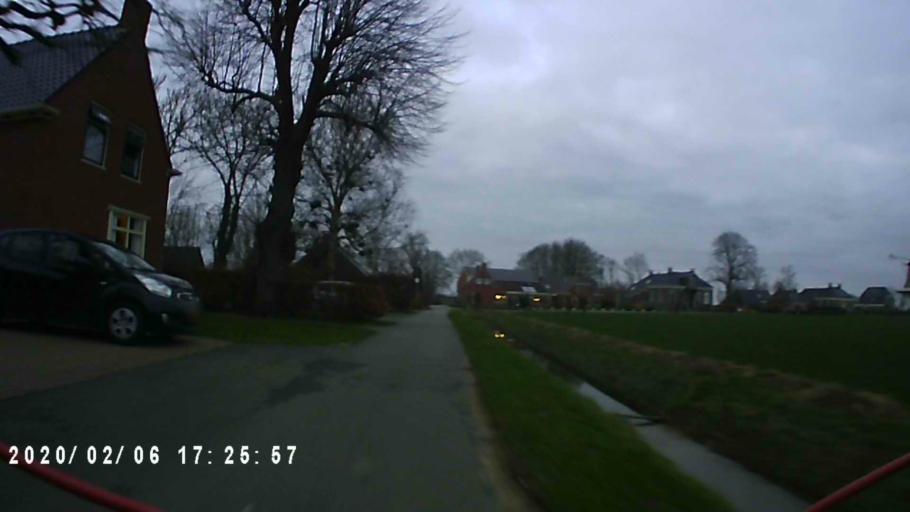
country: NL
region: Groningen
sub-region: Gemeente Winsum
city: Winsum
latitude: 53.2996
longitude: 6.5302
